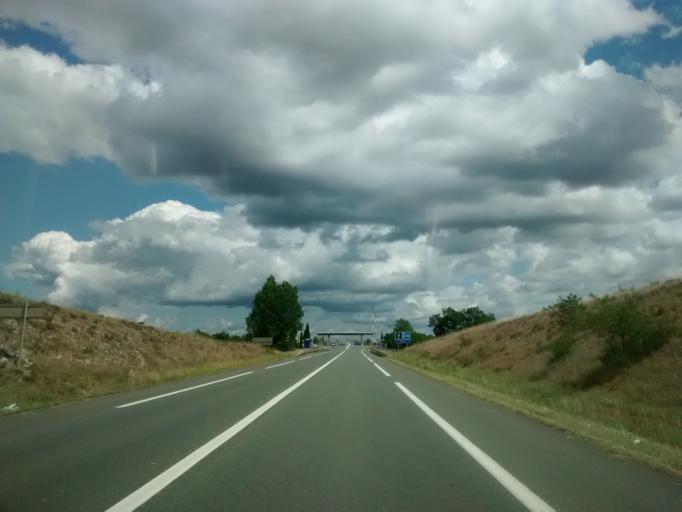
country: FR
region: Midi-Pyrenees
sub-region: Departement du Lot
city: Lalbenque
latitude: 44.3428
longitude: 1.4896
